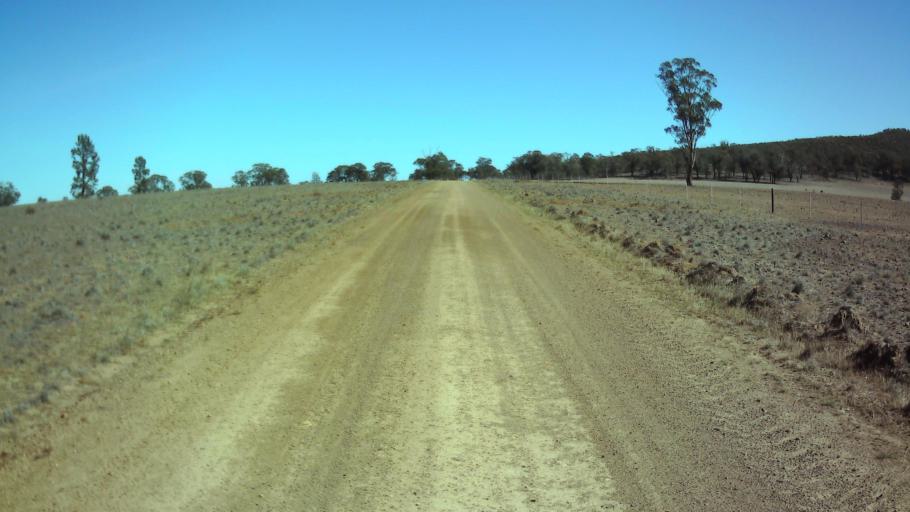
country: AU
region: New South Wales
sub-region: Weddin
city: Grenfell
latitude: -33.7624
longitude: 147.9230
